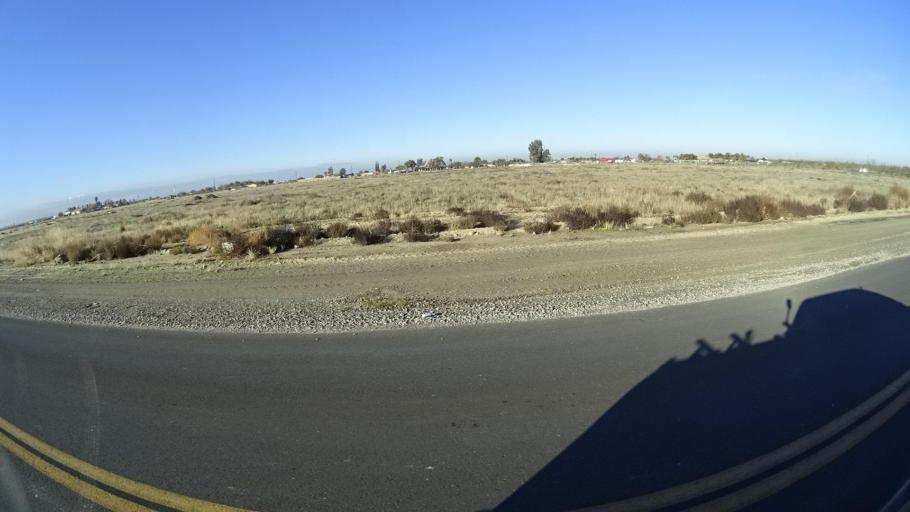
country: US
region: California
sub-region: Kern County
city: Delano
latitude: 35.7730
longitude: -119.2760
